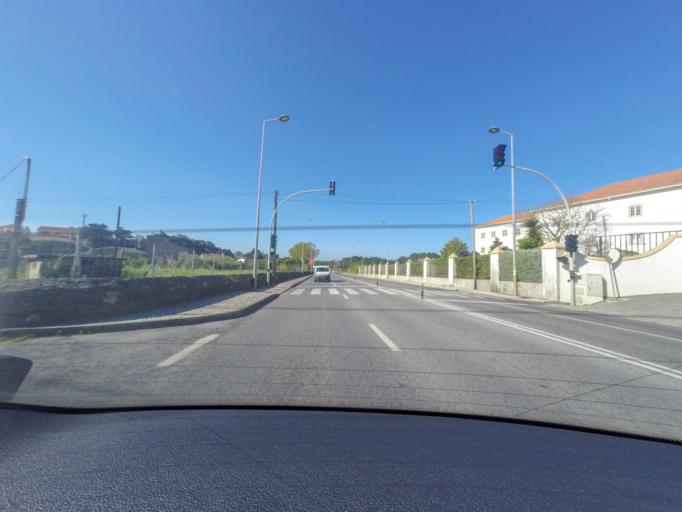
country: PT
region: Lisbon
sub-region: Sintra
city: Sintra
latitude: 38.7690
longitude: -9.3838
